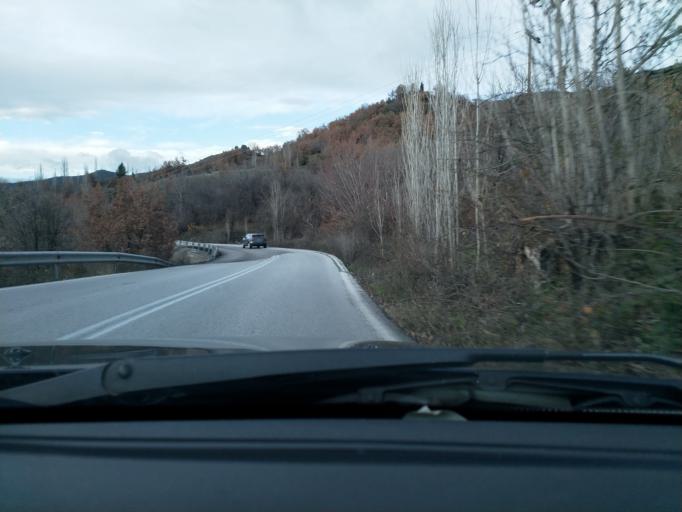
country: GR
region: Epirus
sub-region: Nomos Ioanninon
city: Metsovo
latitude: 39.7898
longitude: 21.3766
